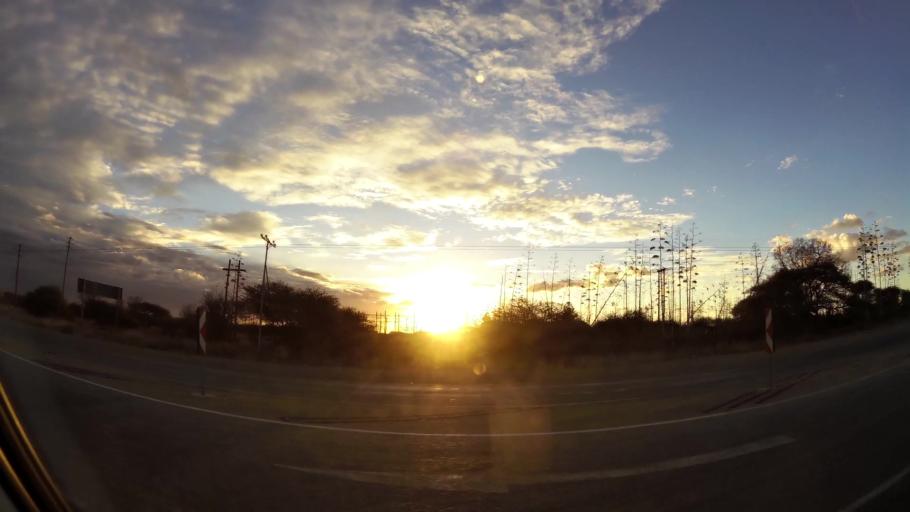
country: ZA
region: Limpopo
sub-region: Capricorn District Municipality
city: Polokwane
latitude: -23.8298
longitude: 29.4906
